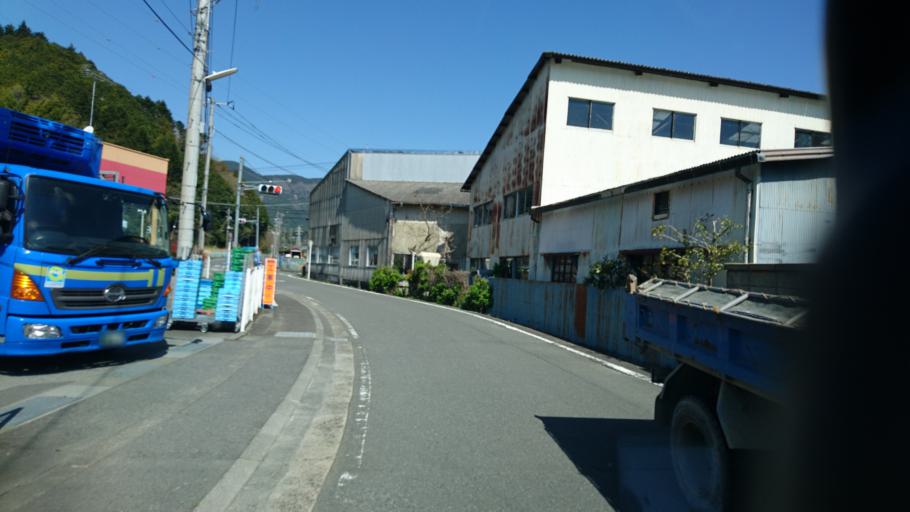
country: JP
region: Shizuoka
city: Fujinomiya
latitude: 35.2805
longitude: 138.4534
